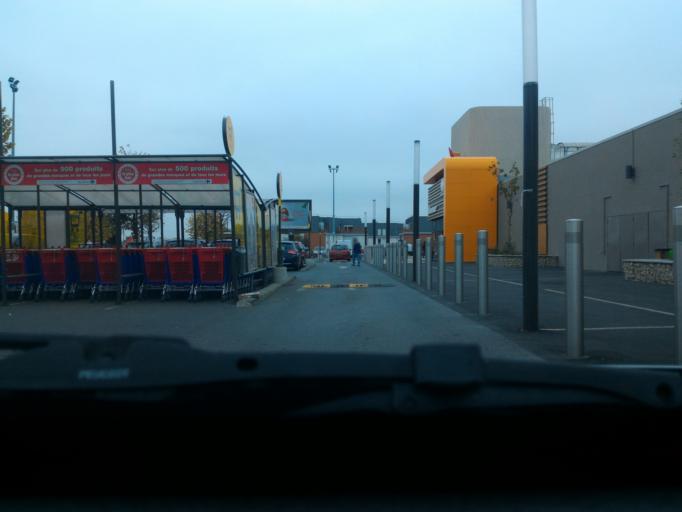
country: FR
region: Ile-de-France
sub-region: Departement du Val-de-Marne
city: L'Hay-les-Roses
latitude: 48.7844
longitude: 2.3453
